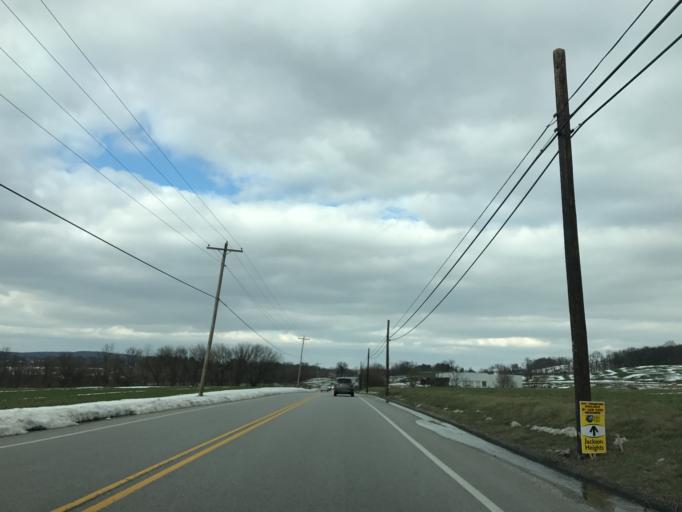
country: US
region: Pennsylvania
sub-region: York County
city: Parkville
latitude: 39.8228
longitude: -76.9367
